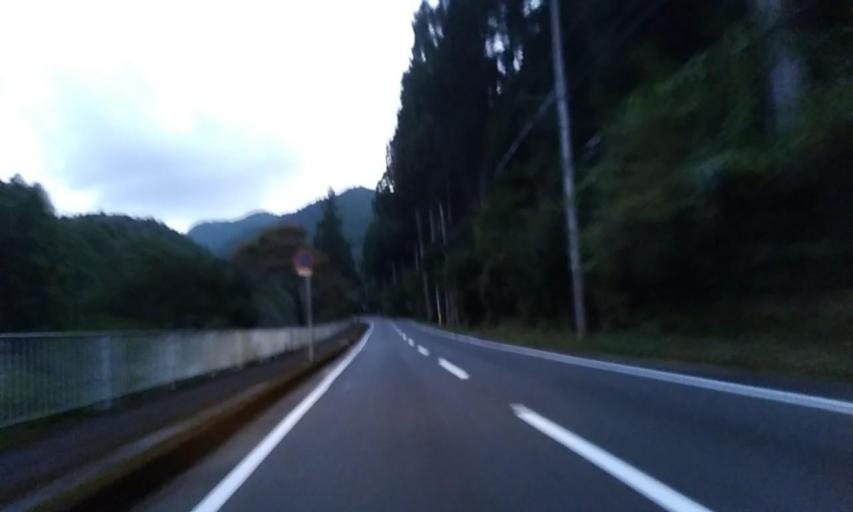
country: JP
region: Wakayama
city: Shingu
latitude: 33.7359
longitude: 135.9306
